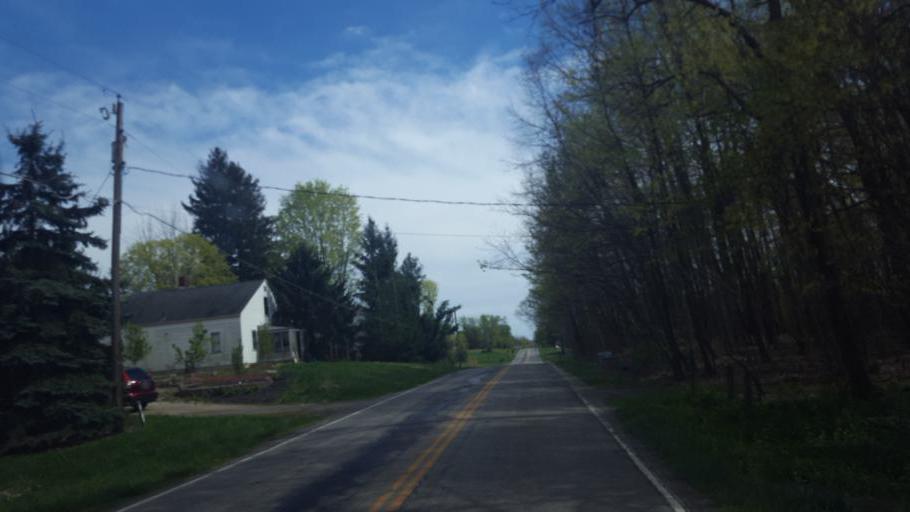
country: US
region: Ohio
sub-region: Richland County
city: Shelby
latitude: 40.8358
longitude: -82.6001
